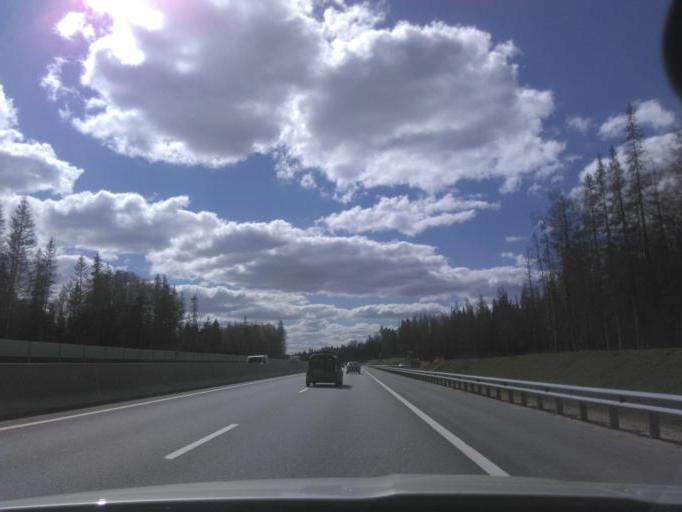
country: RU
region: Moskovskaya
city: Rzhavki
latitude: 56.0338
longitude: 37.2696
